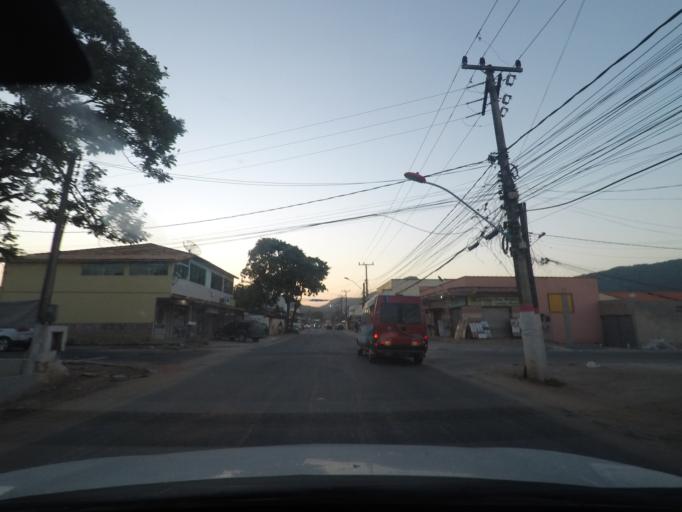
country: BR
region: Rio de Janeiro
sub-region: Niteroi
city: Niteroi
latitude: -22.9622
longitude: -42.9901
